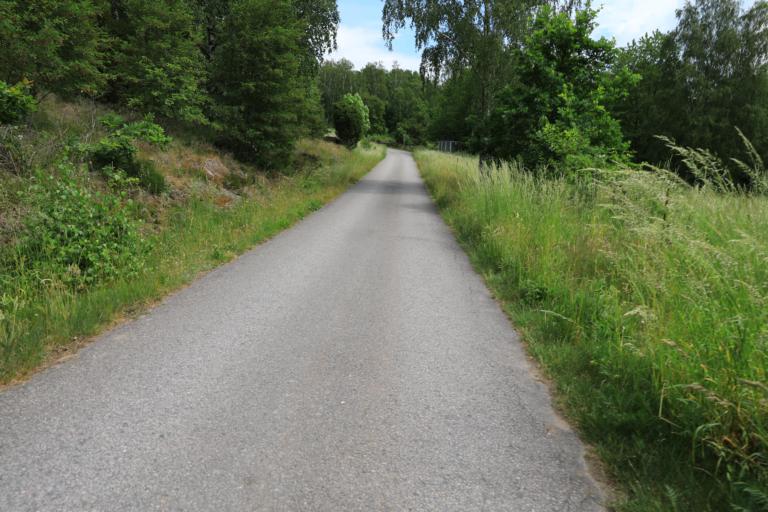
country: SE
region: Halland
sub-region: Varbergs Kommun
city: Varberg
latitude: 57.1655
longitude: 12.2513
